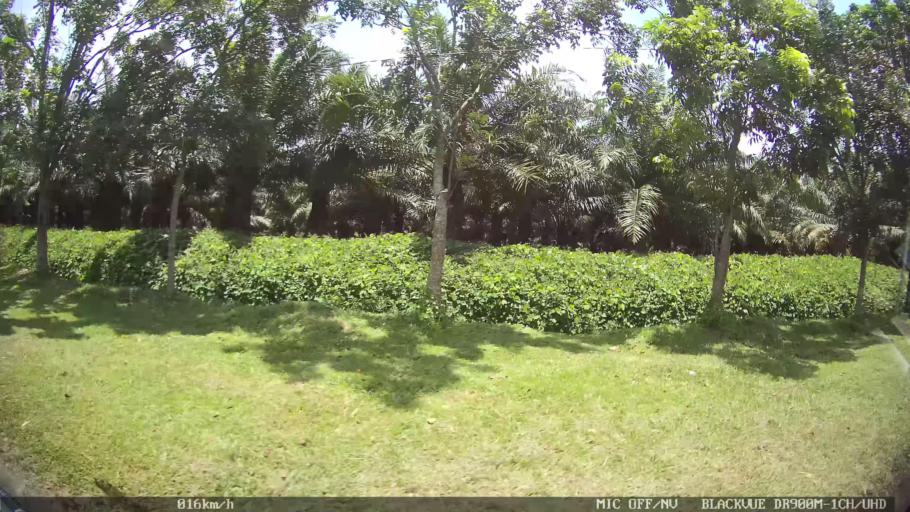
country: ID
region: North Sumatra
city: Percut
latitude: 3.5411
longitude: 98.8718
